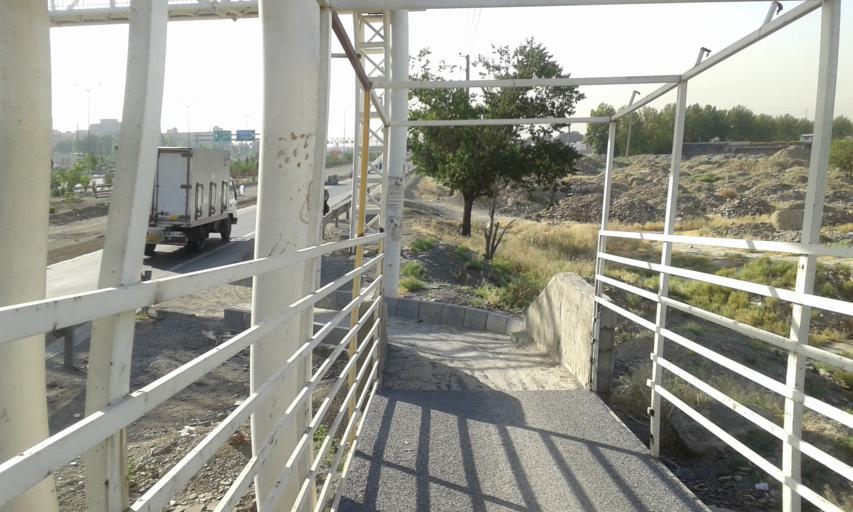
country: IR
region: Tehran
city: Eslamshahr
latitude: 35.6400
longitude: 51.2953
